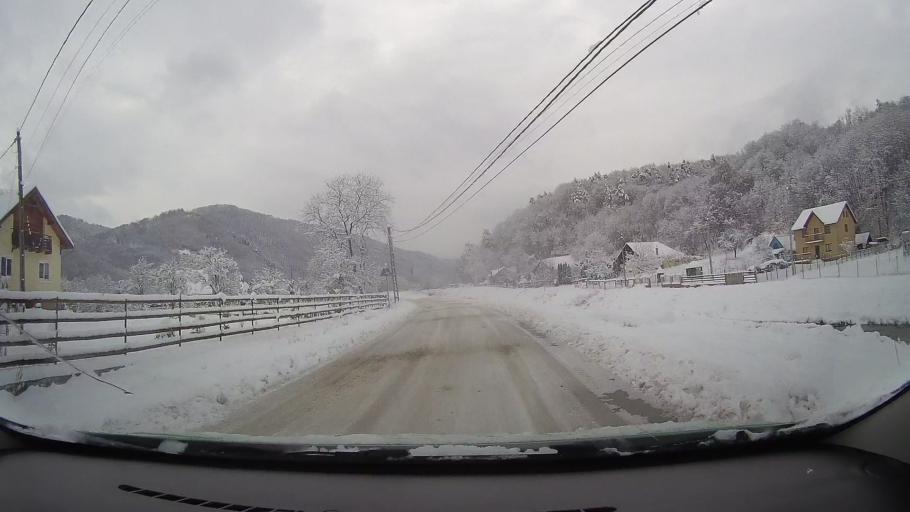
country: RO
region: Alba
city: Pianu de Sus
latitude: 45.8892
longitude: 23.4871
